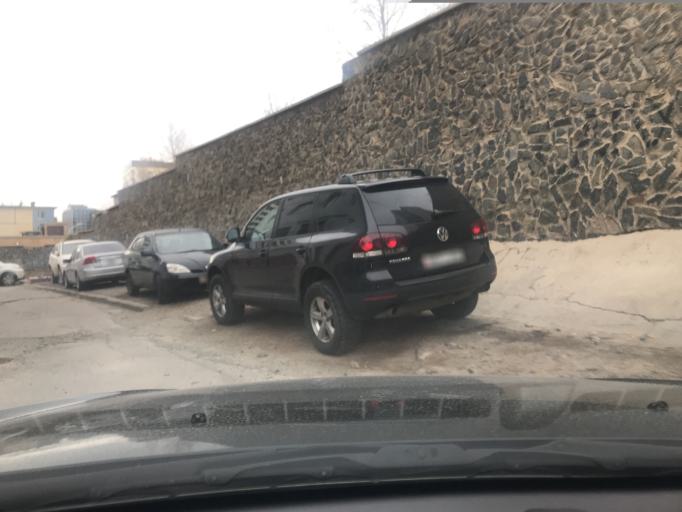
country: MN
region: Ulaanbaatar
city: Ulaanbaatar
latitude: 47.9235
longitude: 106.9412
